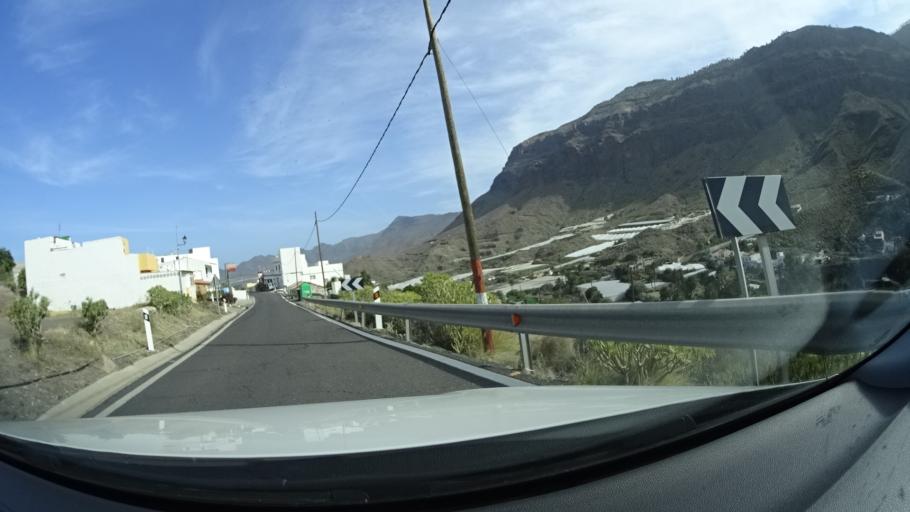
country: ES
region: Canary Islands
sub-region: Provincia de Las Palmas
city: San Nicolas
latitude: 27.9567
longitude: -15.7774
